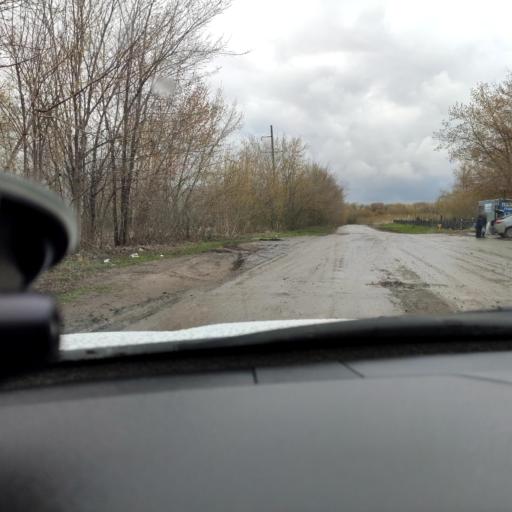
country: RU
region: Samara
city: Smyshlyayevka
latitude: 53.2674
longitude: 50.4861
